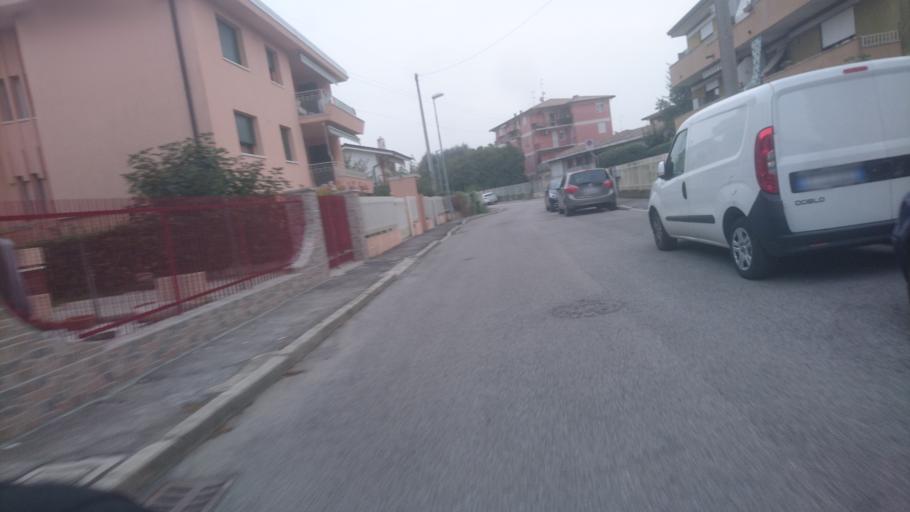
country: IT
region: Veneto
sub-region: Provincia di Padova
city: Tencarola
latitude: 45.3954
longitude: 11.8141
